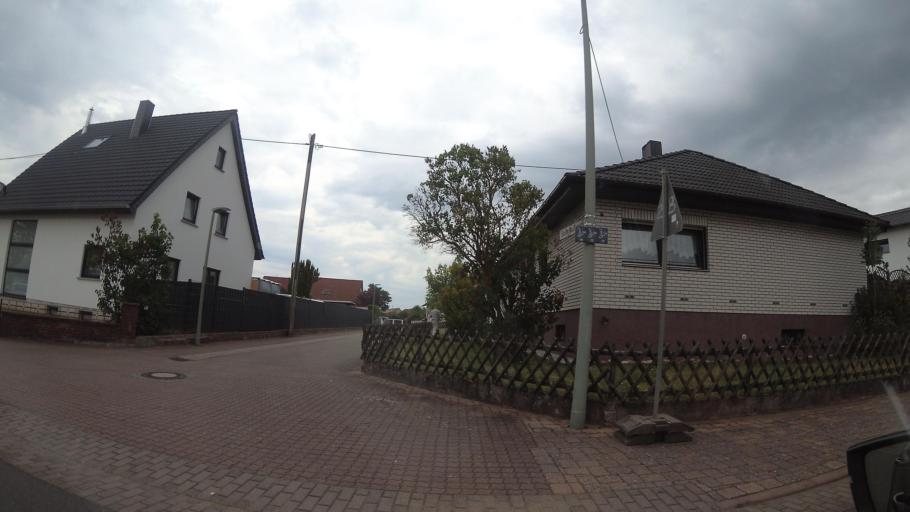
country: DE
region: Rheinland-Pfalz
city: Bruchmuhlbach-Miesau
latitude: 49.4059
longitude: 7.4382
